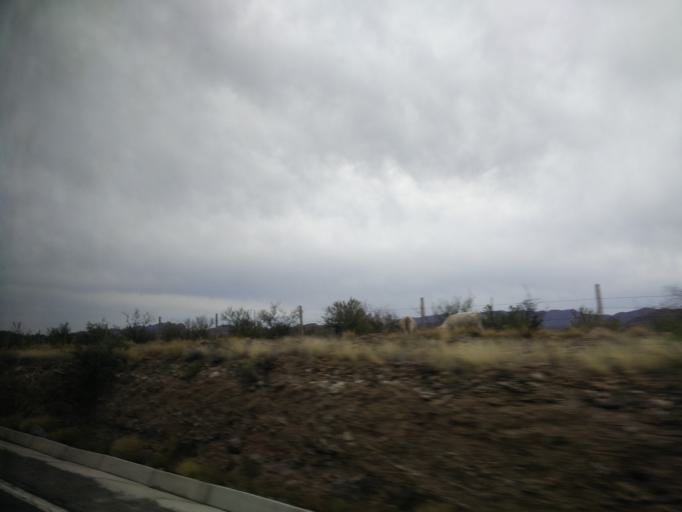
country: MX
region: Sonora
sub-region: Hermosillo
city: Miguel Aleman (La Doce)
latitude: 28.5128
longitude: -111.0455
